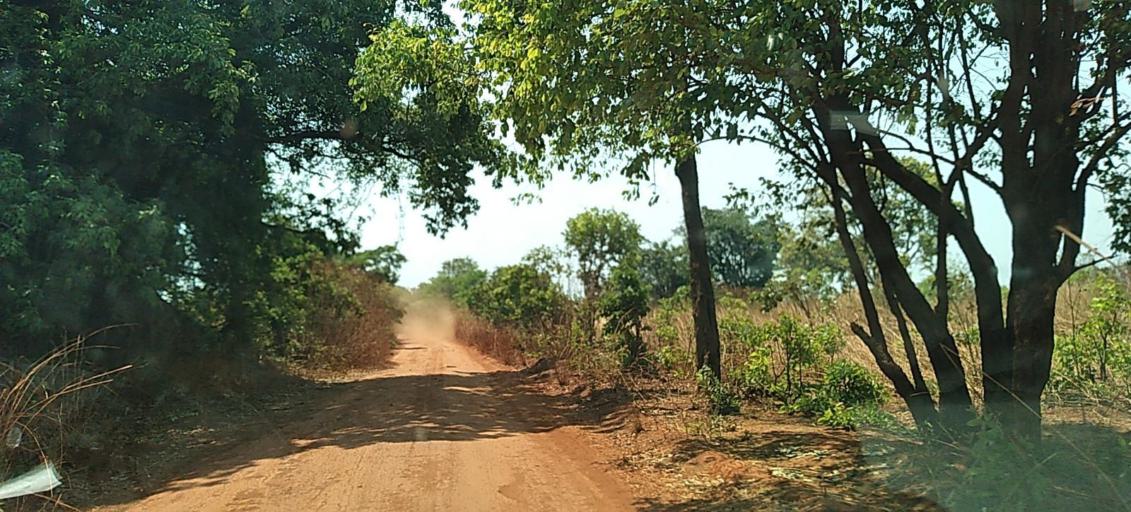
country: ZM
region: North-Western
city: Solwezi
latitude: -12.1278
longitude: 26.3096
